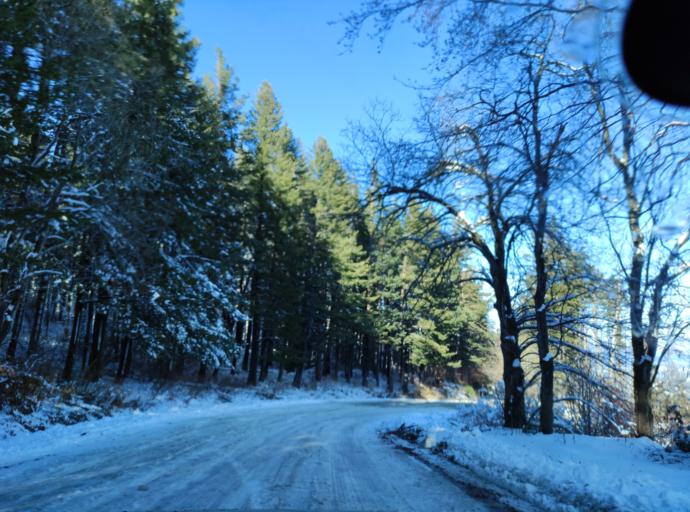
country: BG
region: Sofia-Capital
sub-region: Stolichna Obshtina
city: Sofia
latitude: 42.5901
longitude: 23.3120
